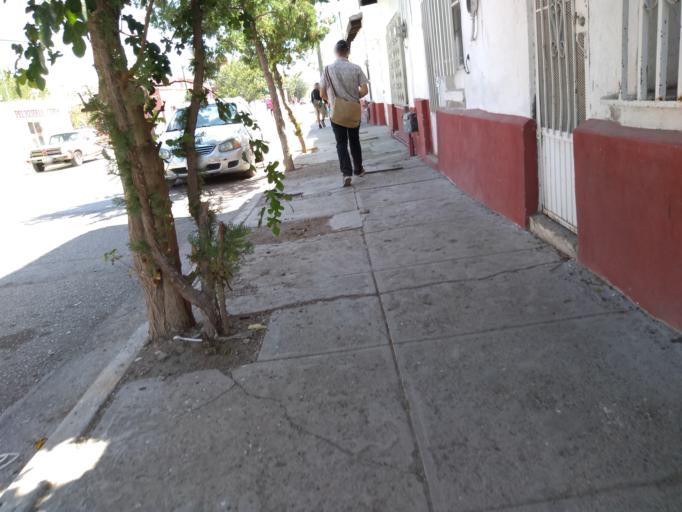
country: US
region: Texas
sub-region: El Paso County
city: El Paso
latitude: 31.7454
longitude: -106.4905
